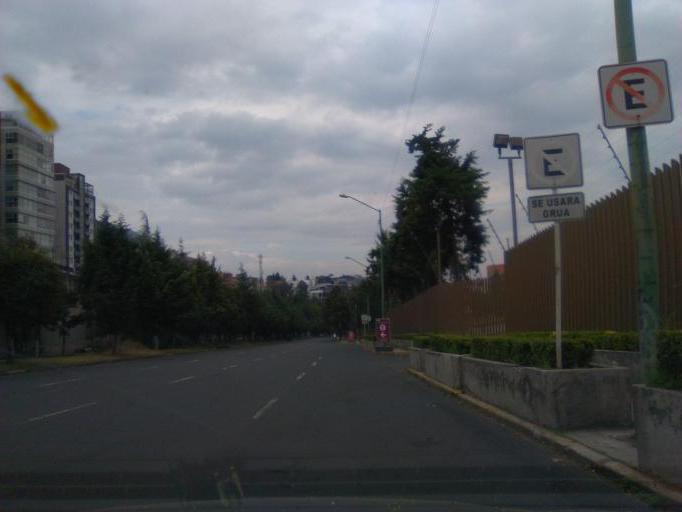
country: MX
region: Mexico City
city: Col. Bosques de las Lomas
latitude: 19.3688
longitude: -99.2660
